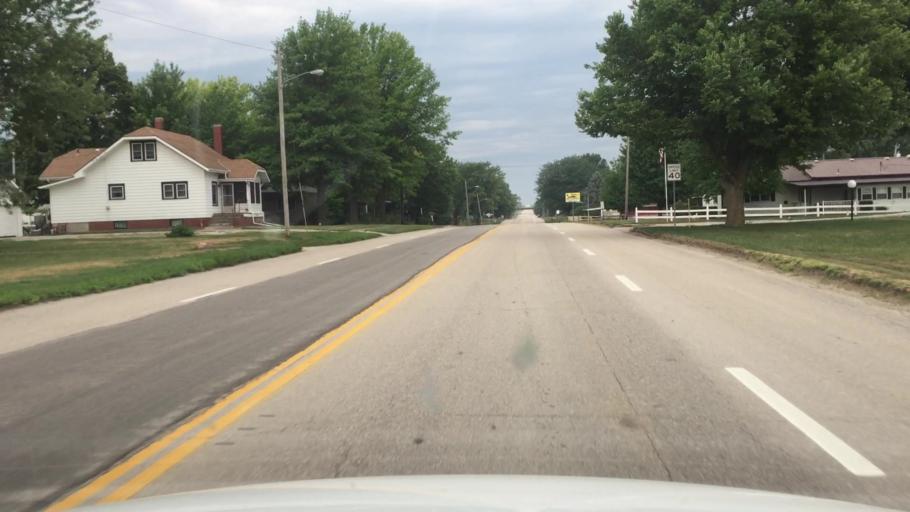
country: US
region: Kansas
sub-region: Nemaha County
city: Sabetha
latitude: 39.8412
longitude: -95.7242
